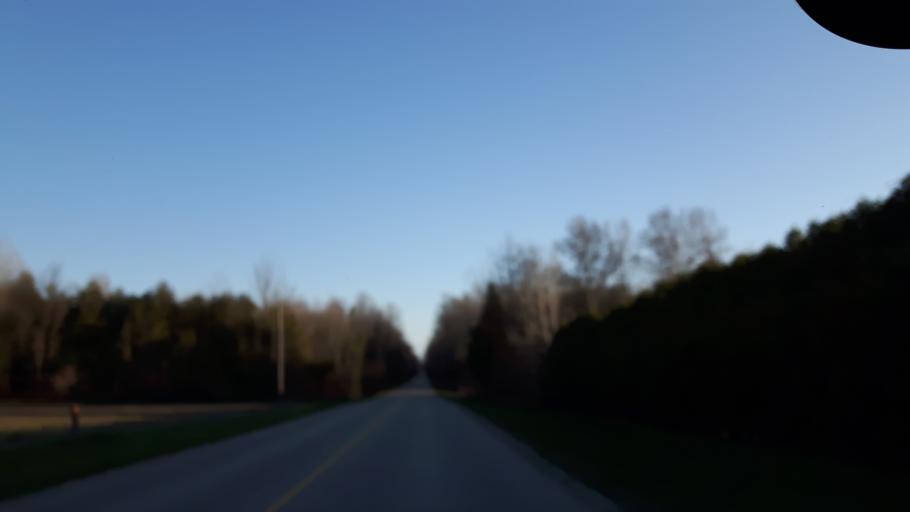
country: CA
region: Ontario
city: Goderich
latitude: 43.6003
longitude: -81.6849
